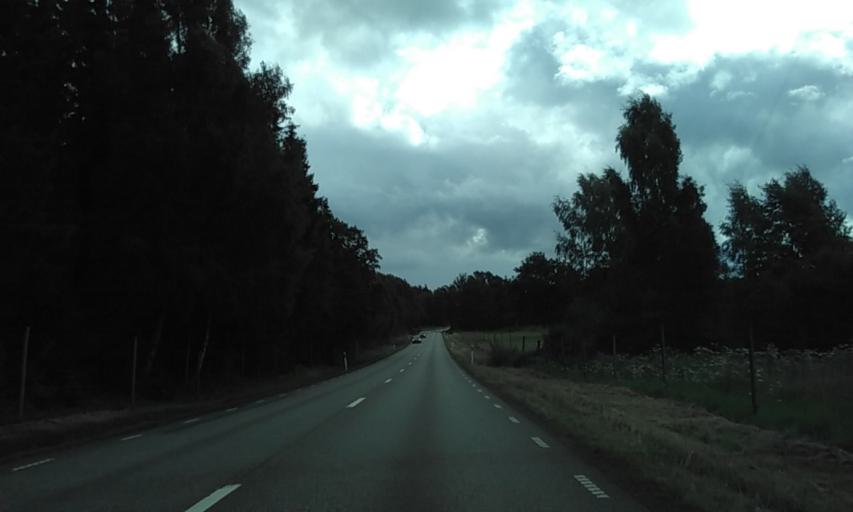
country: SE
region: Vaestra Goetaland
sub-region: Alingsas Kommun
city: Alingsas
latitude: 57.9614
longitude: 12.4465
